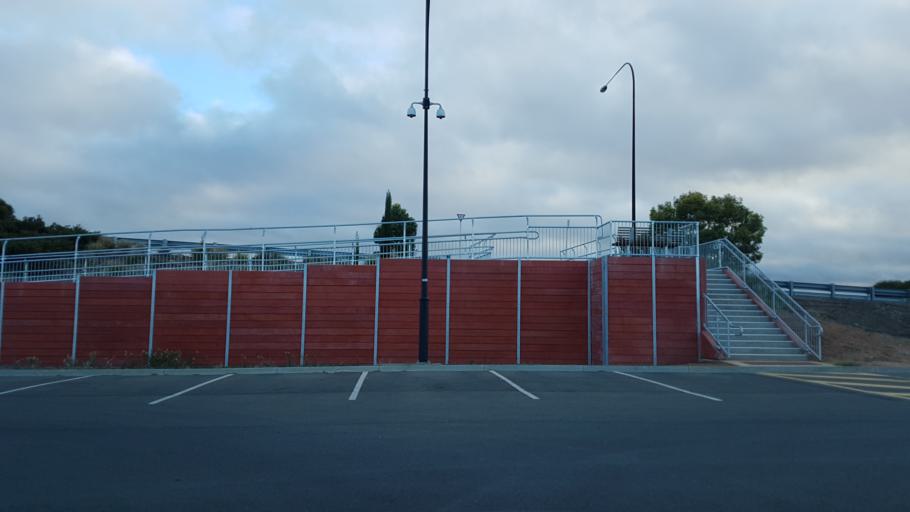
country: AU
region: South Australia
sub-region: Salisbury
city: Ingle Farm
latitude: -34.8048
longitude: 138.6140
